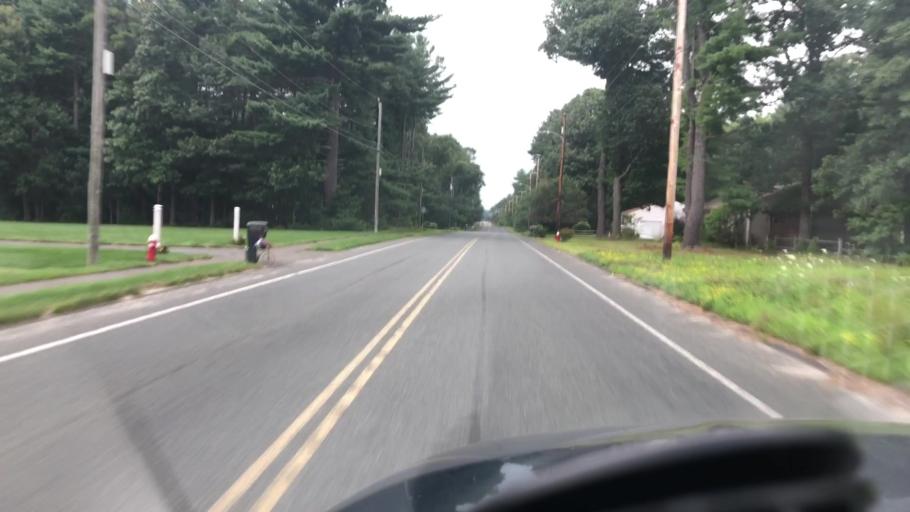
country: US
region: Massachusetts
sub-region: Hampshire County
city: Southampton
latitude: 42.1957
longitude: -72.6874
